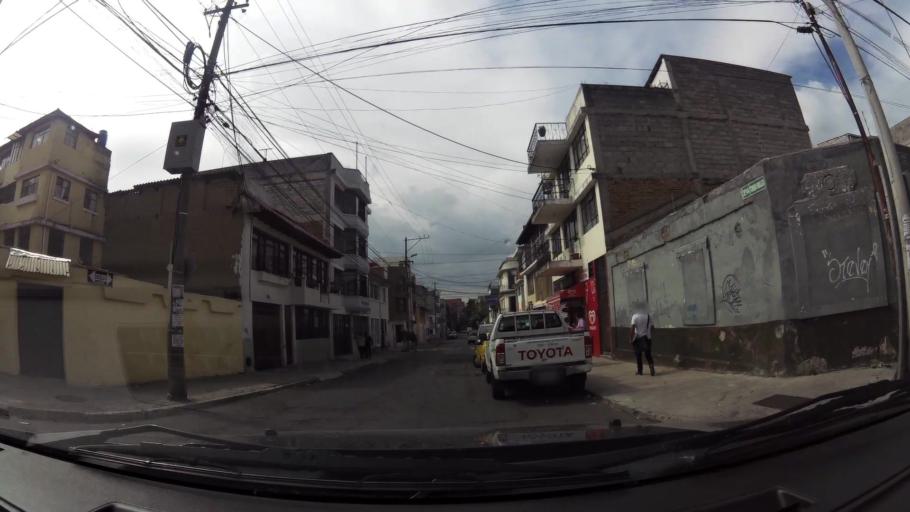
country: EC
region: Pichincha
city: Quito
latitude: -0.2164
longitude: -78.4883
